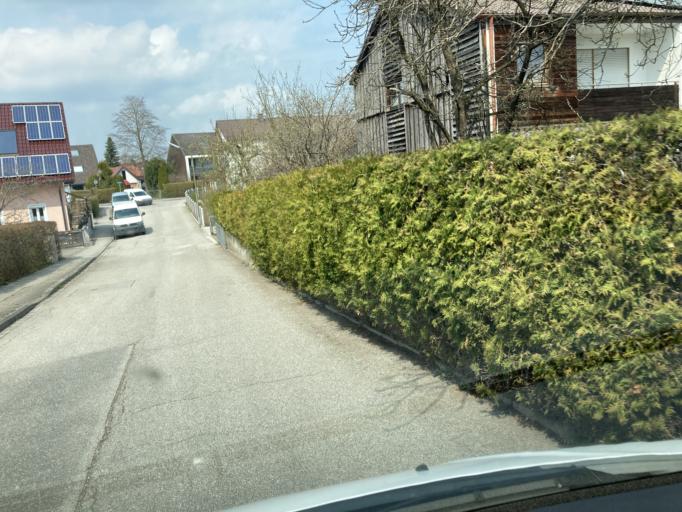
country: DE
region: Bavaria
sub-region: Upper Bavaria
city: Grafing bei Munchen
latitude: 48.0407
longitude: 11.9643
